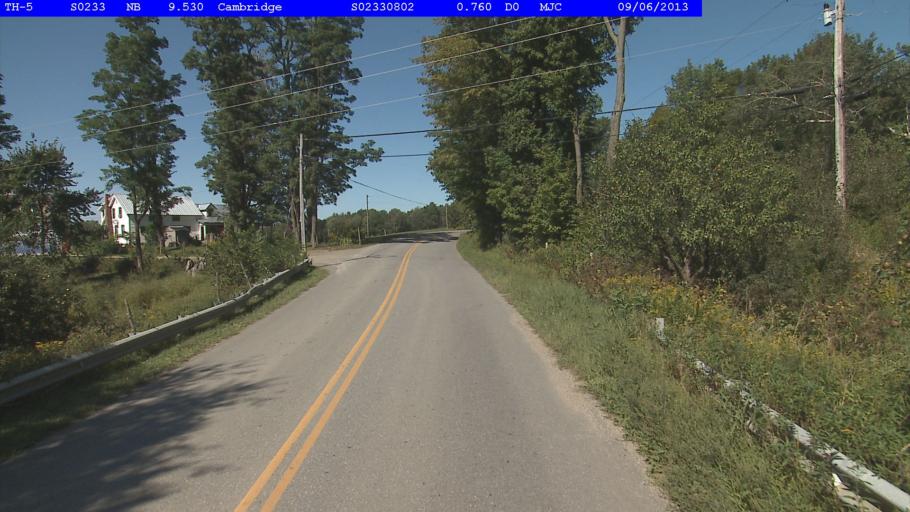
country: US
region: Vermont
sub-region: Chittenden County
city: Jericho
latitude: 44.5939
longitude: -72.8589
